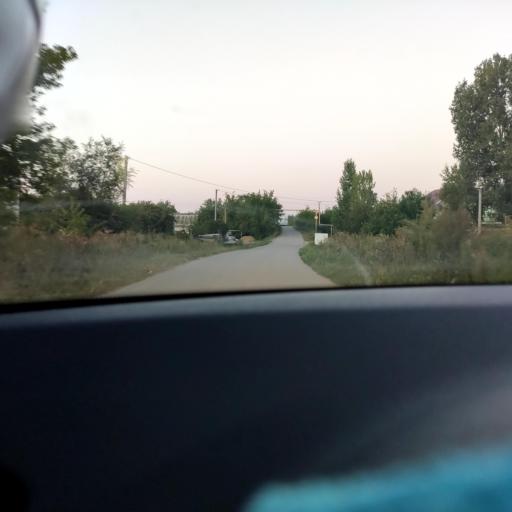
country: RU
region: Samara
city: Novokuybyshevsk
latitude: 53.0735
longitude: 50.0118
